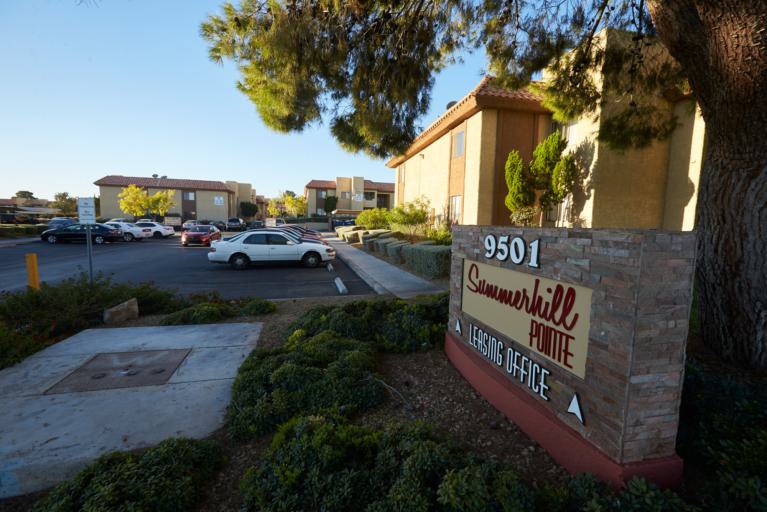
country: US
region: Nevada
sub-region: Clark County
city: Summerlin South
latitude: 36.1442
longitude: -115.3001
